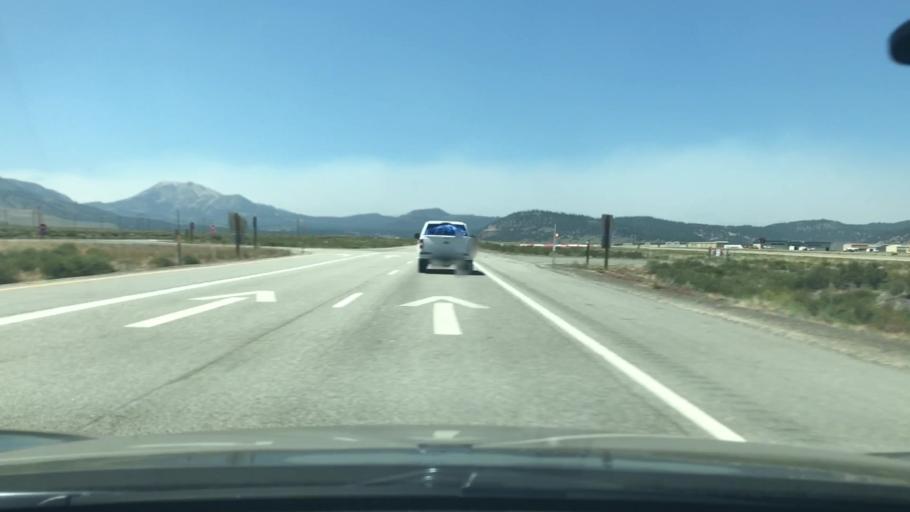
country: US
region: California
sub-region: Mono County
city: Mammoth Lakes
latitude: 37.6227
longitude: -118.8389
